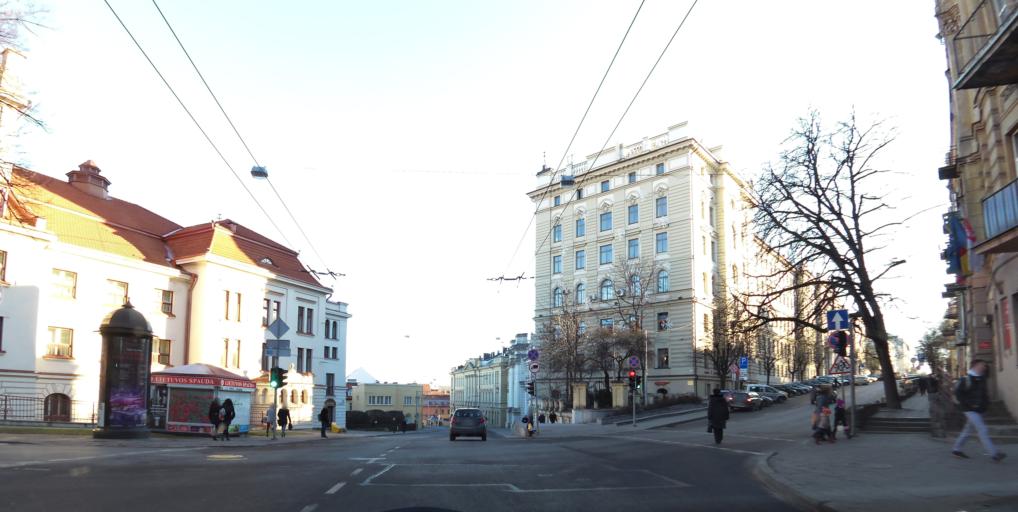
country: LT
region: Vilnius County
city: Naujamiestis
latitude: 54.6809
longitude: 25.2725
